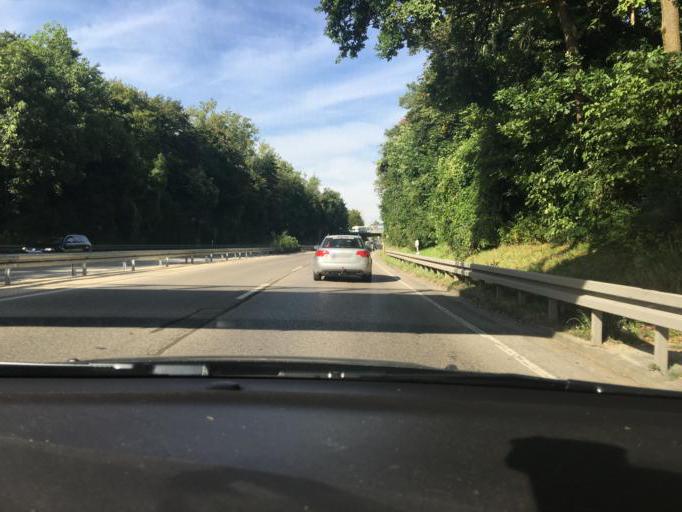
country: DE
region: Bavaria
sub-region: Upper Bavaria
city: Unterfoehring
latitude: 48.1732
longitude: 11.6337
